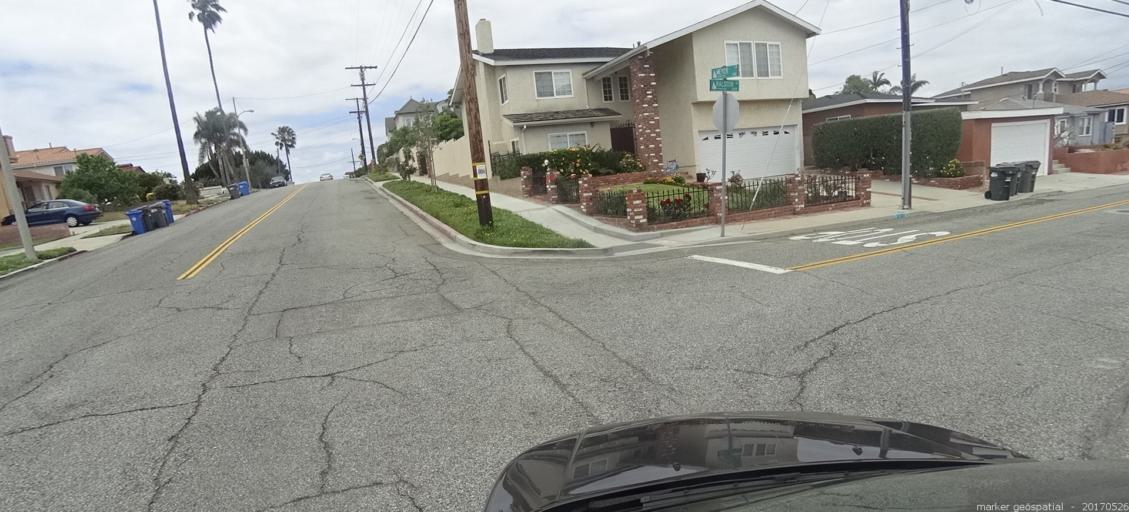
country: US
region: California
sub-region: Los Angeles County
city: Redondo Beach
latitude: 33.8619
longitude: -118.3699
